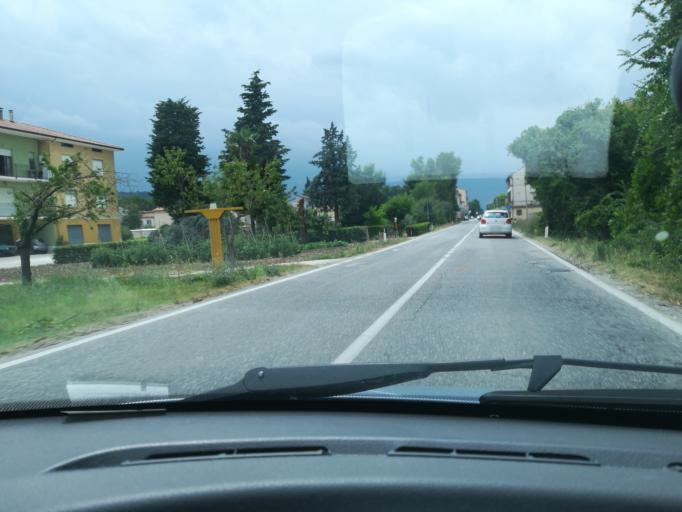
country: IT
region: The Marches
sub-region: Provincia di Macerata
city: Montecassiano
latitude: 43.3483
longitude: 13.4612
